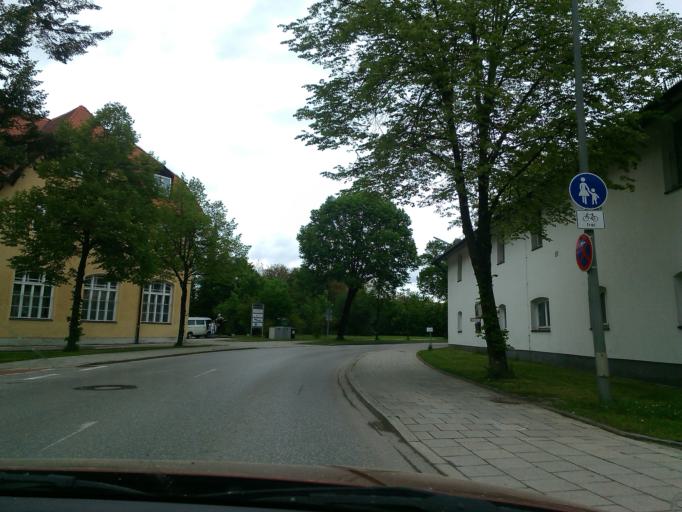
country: DE
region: Bavaria
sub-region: Upper Bavaria
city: Planegg
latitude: 48.1012
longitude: 11.4238
